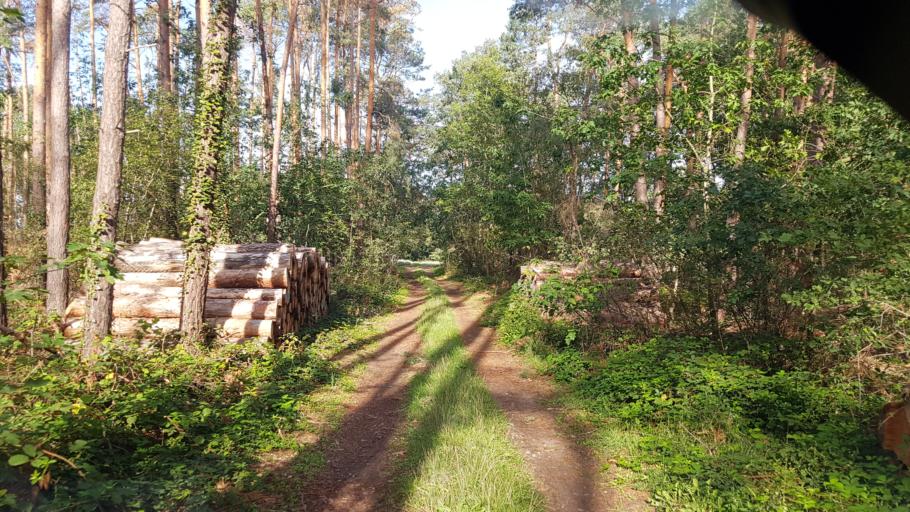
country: DE
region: Brandenburg
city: Sonnewalde
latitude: 51.6710
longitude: 13.6766
